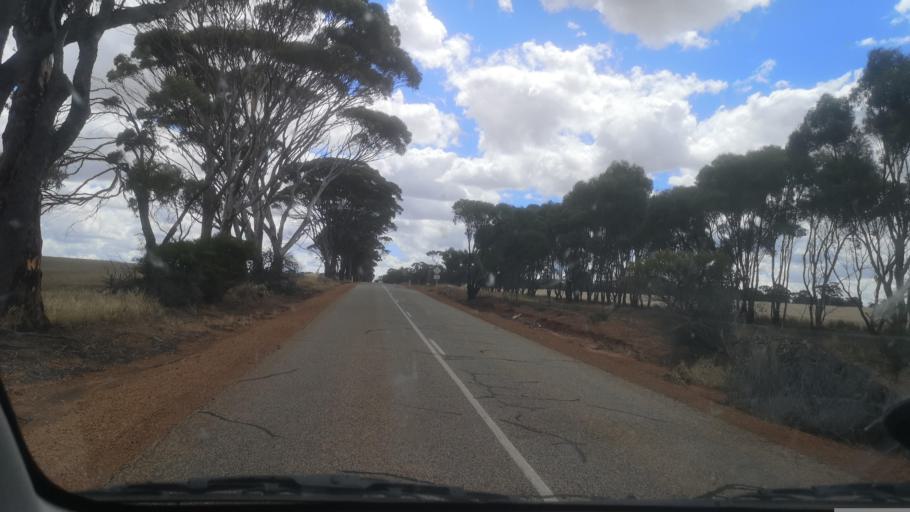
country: AU
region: Western Australia
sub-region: Beverley
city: Beverley
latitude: -31.9899
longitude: 117.1187
